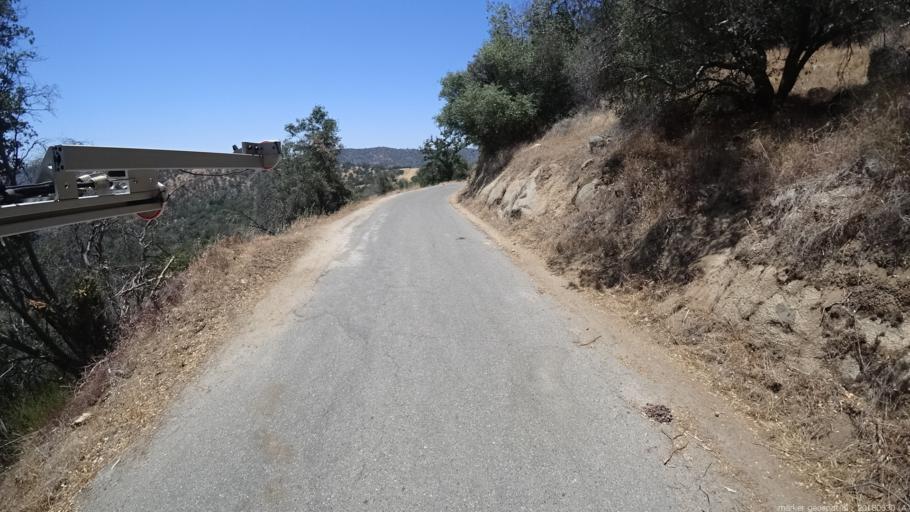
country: US
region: California
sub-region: Fresno County
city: Auberry
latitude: 37.1641
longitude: -119.4472
